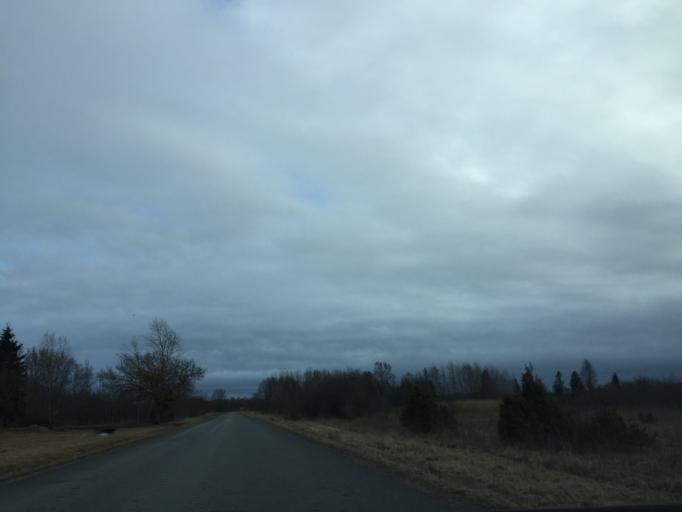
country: EE
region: Laeaene
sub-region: Haapsalu linn
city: Haapsalu
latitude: 58.8146
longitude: 23.5505
